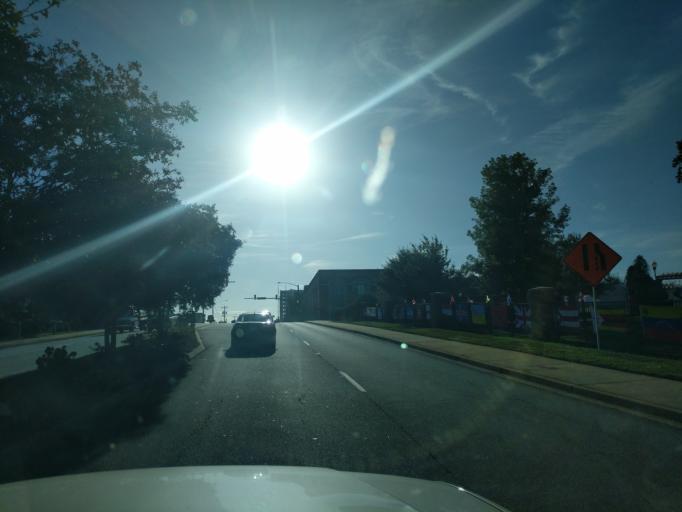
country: US
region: South Carolina
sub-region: Spartanburg County
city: Spartanburg
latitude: 34.9533
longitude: -81.9278
